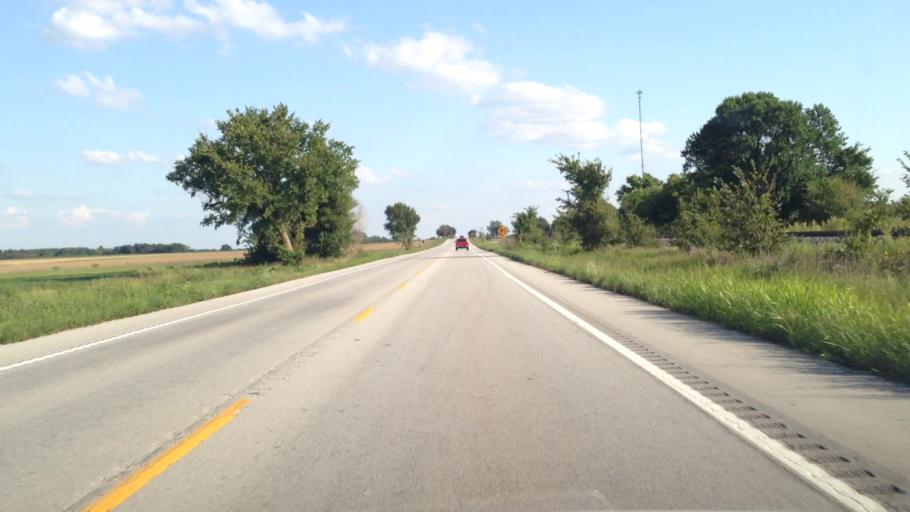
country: US
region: Missouri
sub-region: Jasper County
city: Carl Junction
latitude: 37.2667
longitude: -94.5971
